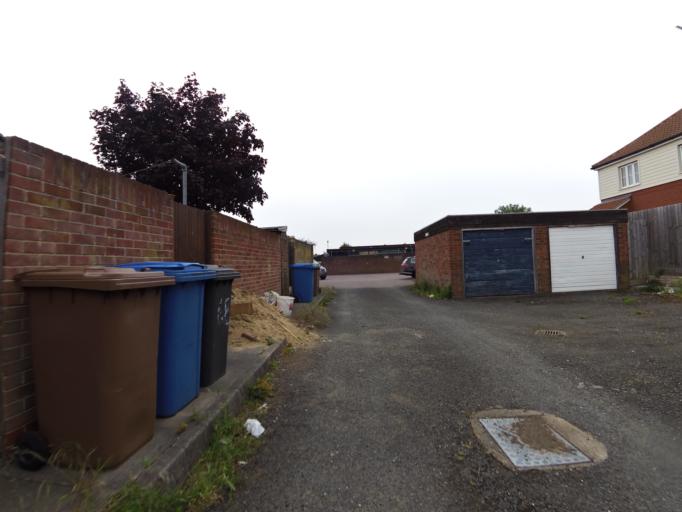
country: GB
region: England
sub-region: Suffolk
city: Ipswich
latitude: 52.0820
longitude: 1.1459
